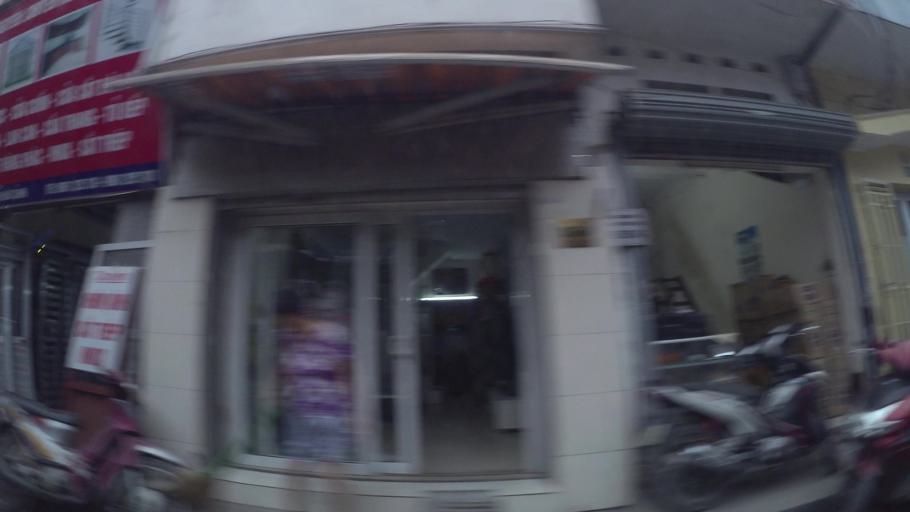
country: VN
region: Ha Noi
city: Hai BaTrung
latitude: 20.9870
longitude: 105.8526
